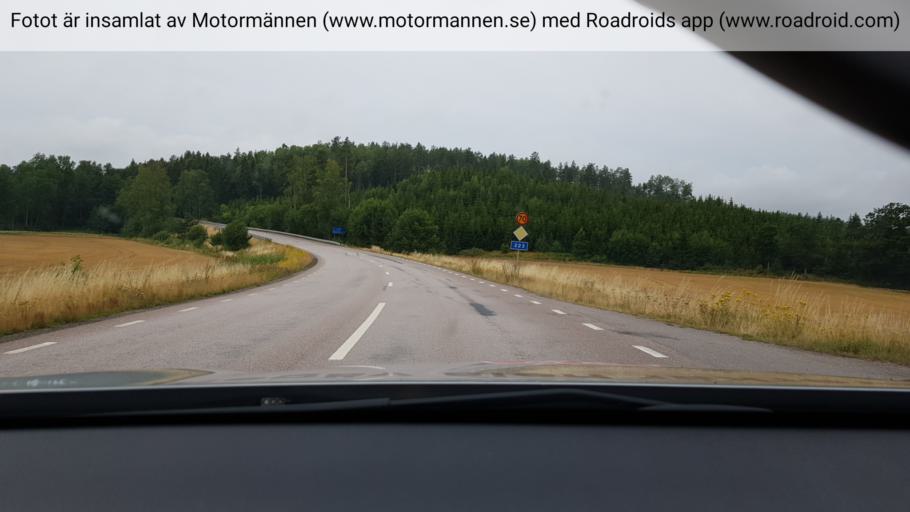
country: SE
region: Soedermanland
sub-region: Strangnas Kommun
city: Mariefred
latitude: 59.2386
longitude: 17.1760
